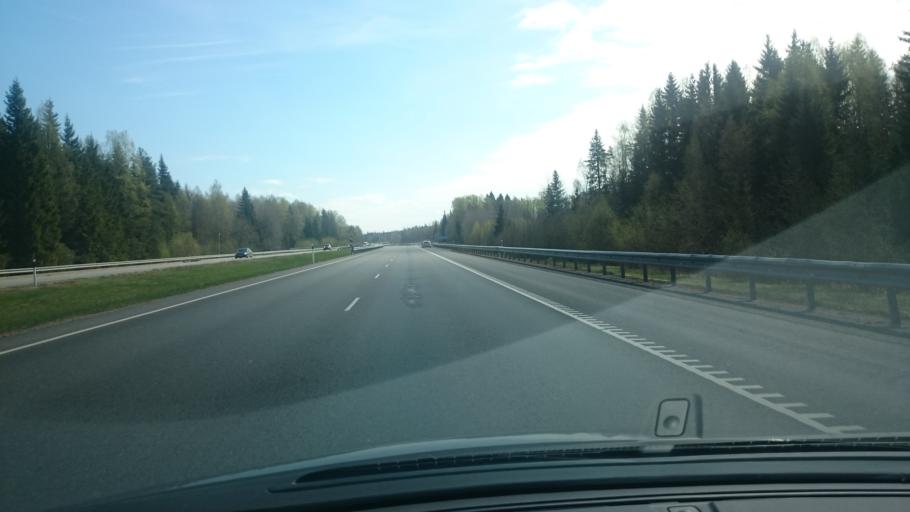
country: EE
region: Harju
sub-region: Loksa linn
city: Loksa
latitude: 59.4620
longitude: 25.7674
